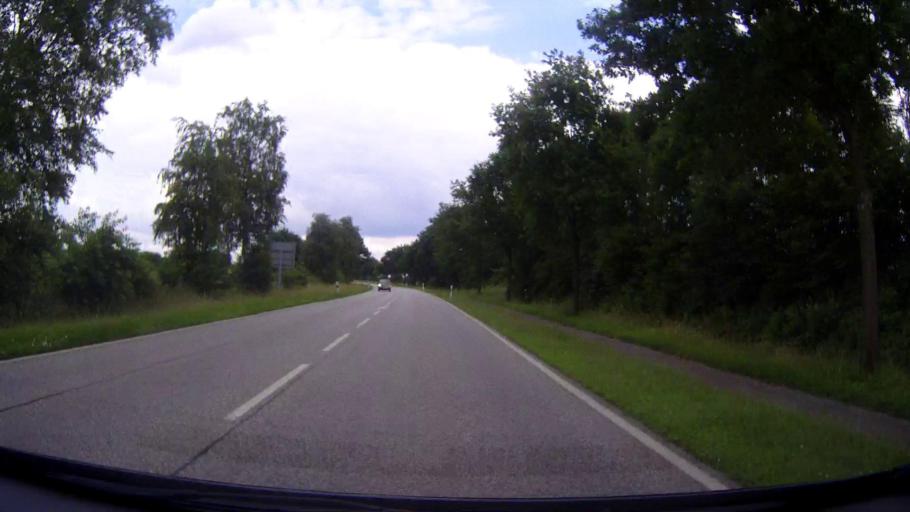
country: DE
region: Schleswig-Holstein
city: Beldorf
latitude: 54.1210
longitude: 9.3446
